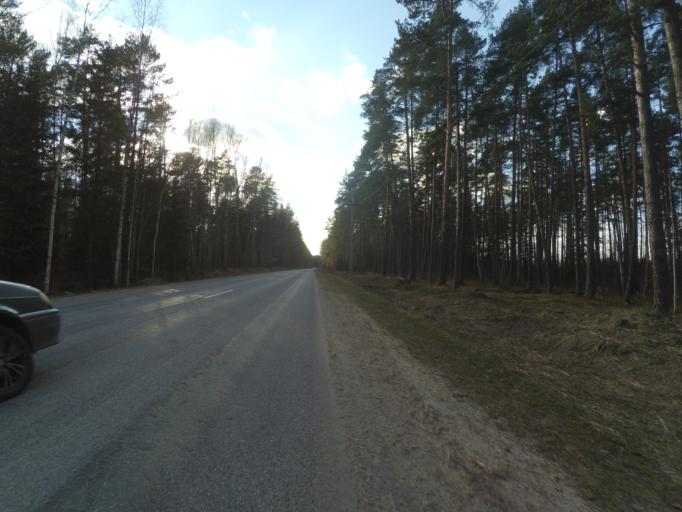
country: RU
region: Moskovskaya
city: Pushchino
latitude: 54.9043
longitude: 37.7017
